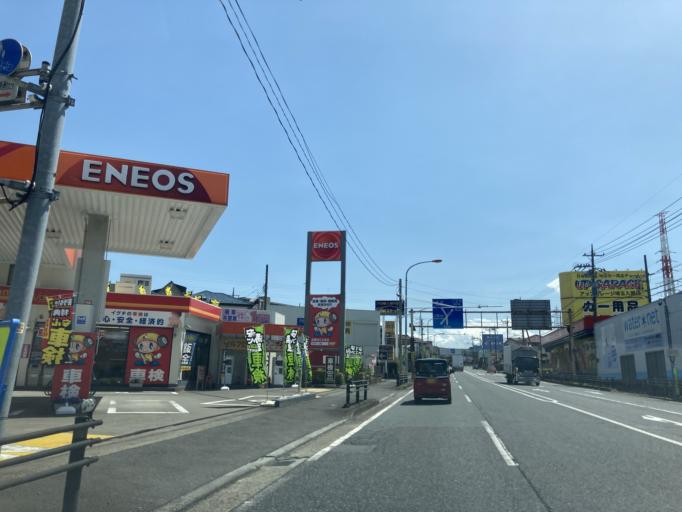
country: JP
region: Saitama
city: Sayama
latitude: 35.8281
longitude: 139.3806
